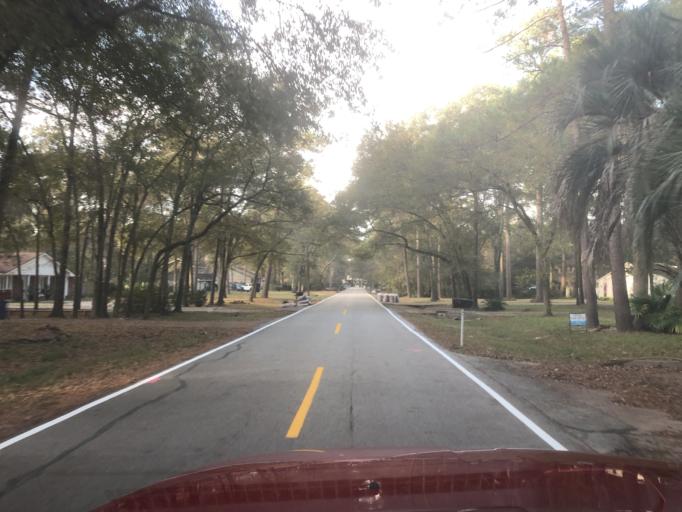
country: US
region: Texas
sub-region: Harris County
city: Spring
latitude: 30.0204
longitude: -95.4754
